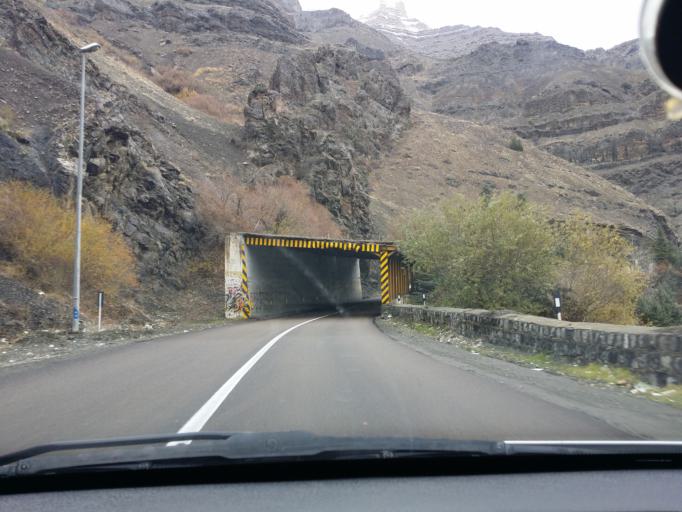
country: IR
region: Alborz
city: Karaj
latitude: 36.0001
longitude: 51.1138
